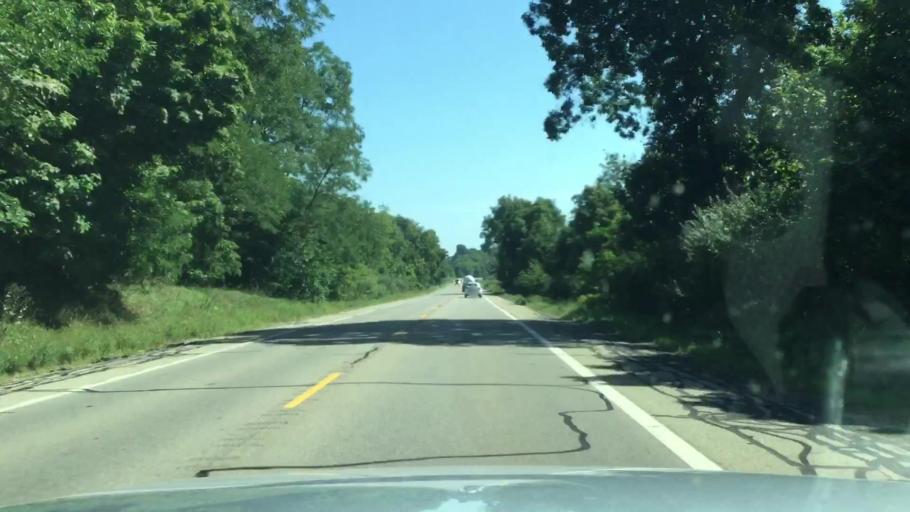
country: US
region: Michigan
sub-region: Lenawee County
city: Clinton
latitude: 42.0732
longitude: -84.0337
